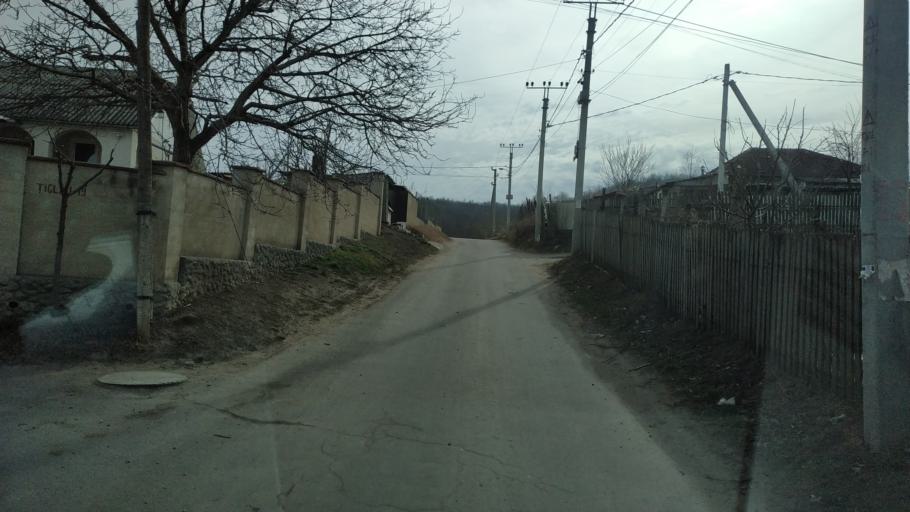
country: MD
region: Chisinau
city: Vatra
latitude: 47.0870
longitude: 28.7724
